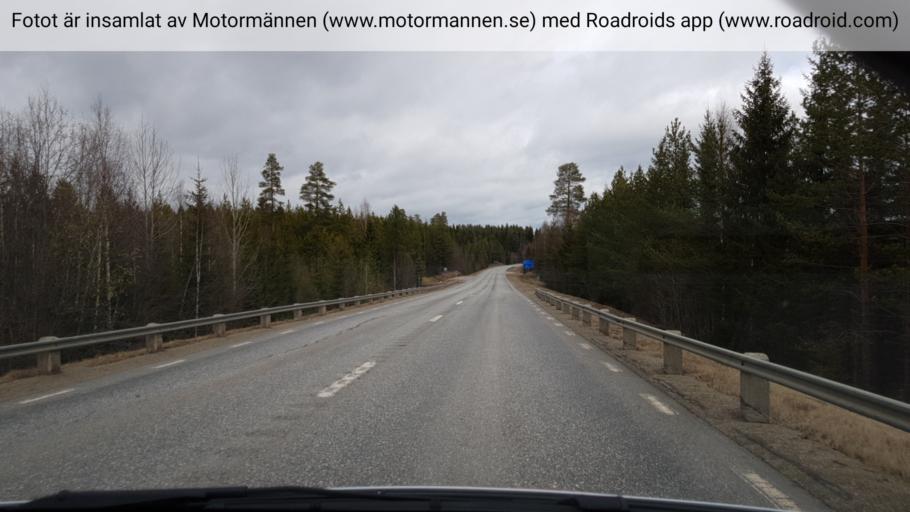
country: SE
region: Vaesterbotten
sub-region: Bjurholms Kommun
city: Bjurholm
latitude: 63.9233
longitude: 19.1856
